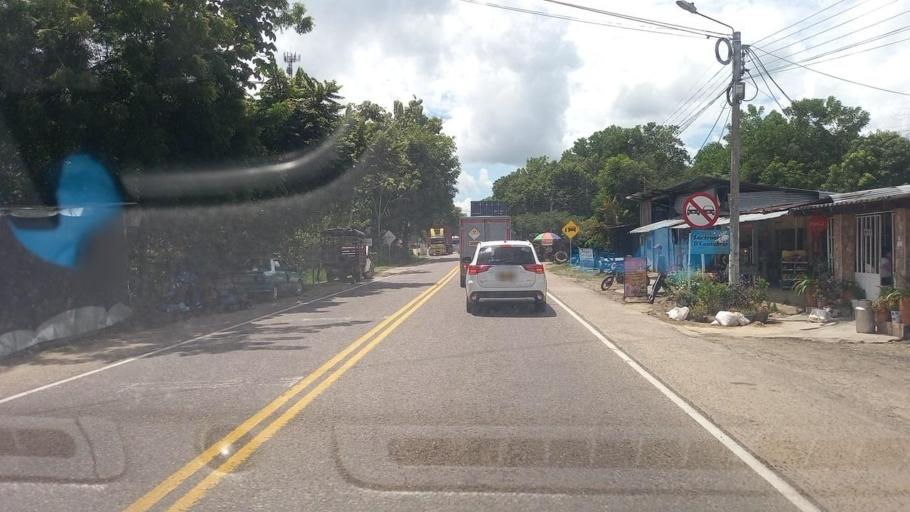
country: CO
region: Santander
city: Puerto Parra
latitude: 6.6469
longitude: -73.9511
